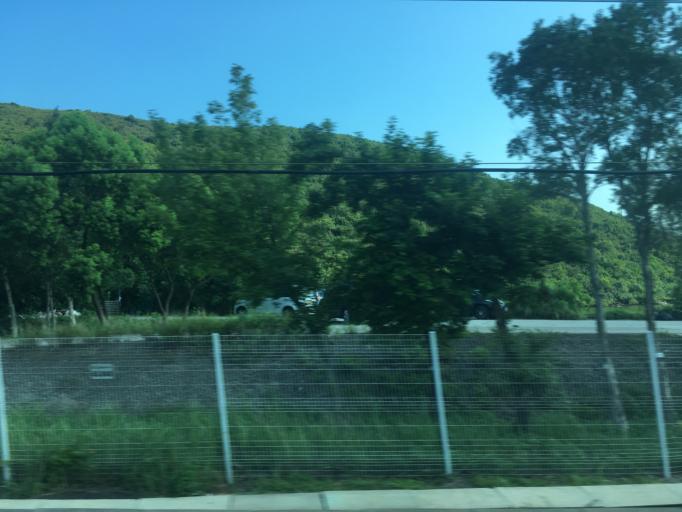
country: HK
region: Tuen Mun
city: Tuen Mun
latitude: 22.3256
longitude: 114.0212
